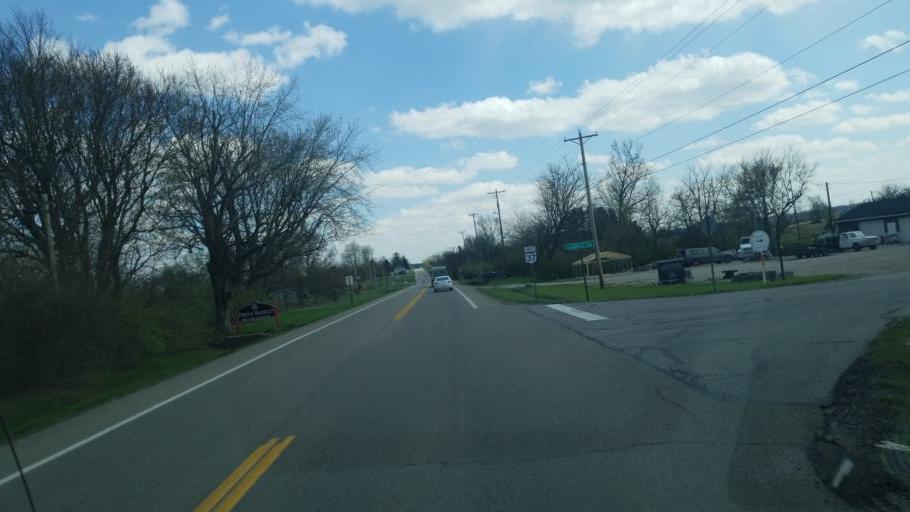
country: US
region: Ohio
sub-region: Licking County
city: Johnstown
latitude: 40.1445
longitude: -82.6761
